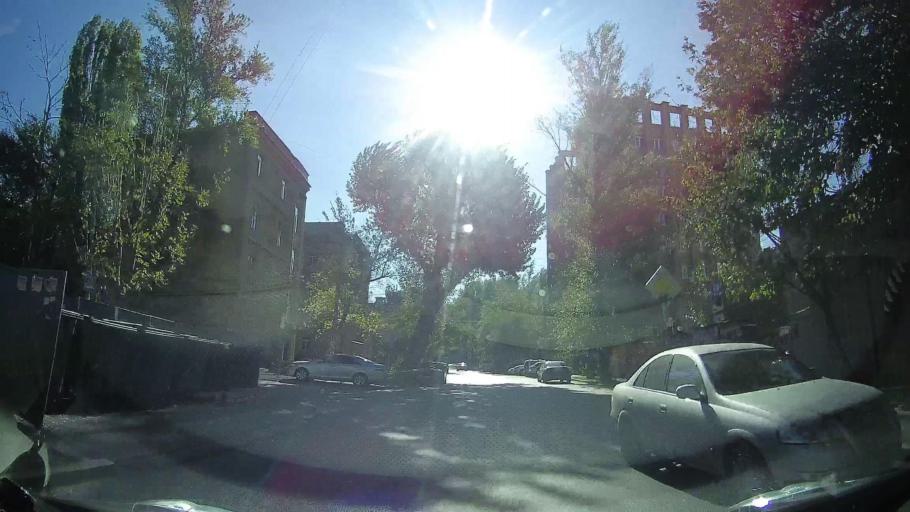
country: RU
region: Rostov
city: Rostov-na-Donu
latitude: 47.2315
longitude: 39.7317
